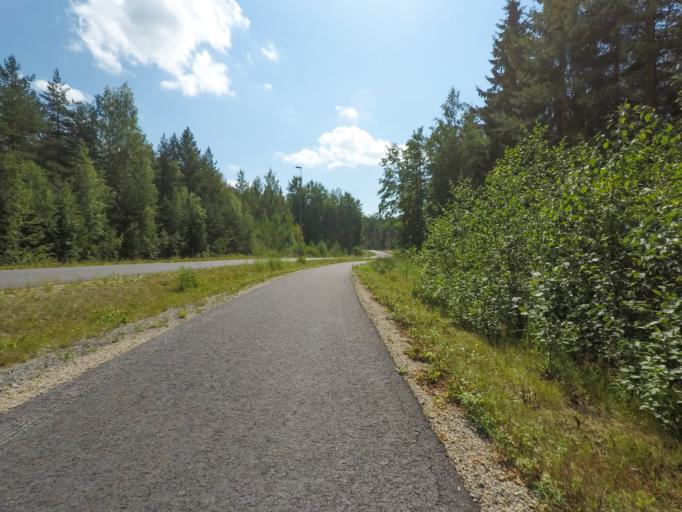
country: FI
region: Southern Savonia
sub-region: Mikkeli
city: Puumala
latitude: 61.5088
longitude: 28.1691
